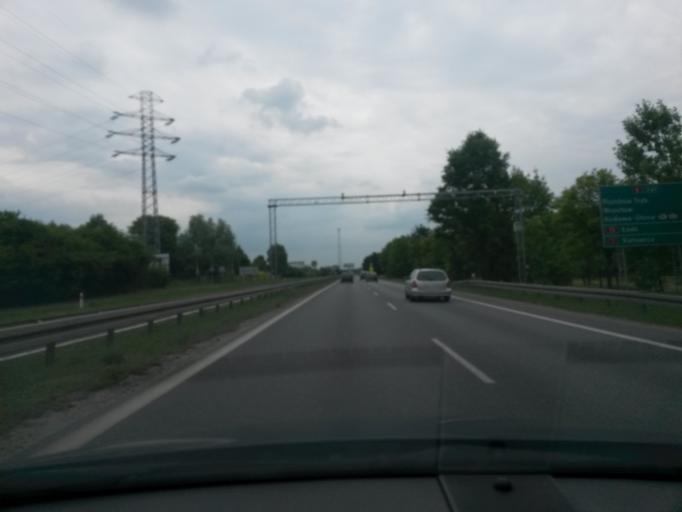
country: PL
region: Masovian Voivodeship
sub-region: Powiat pruszkowski
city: Nadarzyn
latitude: 52.0920
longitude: 20.8114
